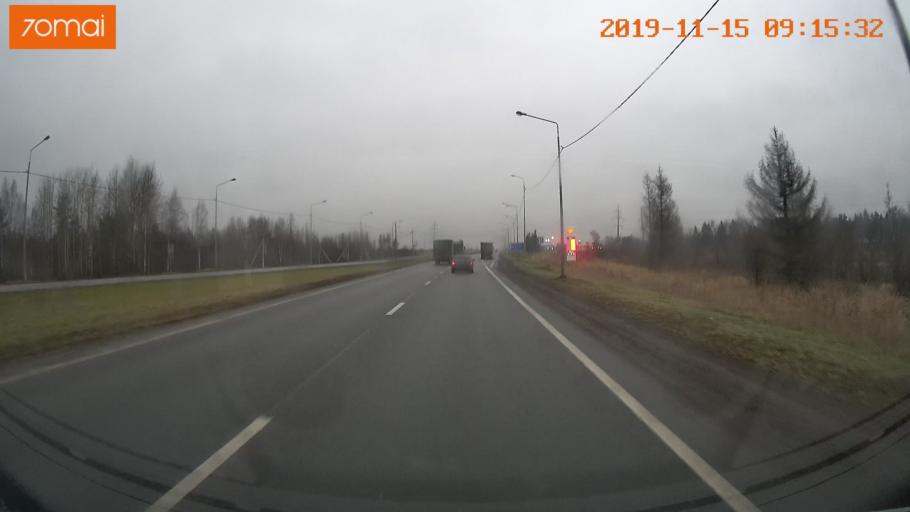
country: RU
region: Vologda
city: Tonshalovo
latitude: 59.2400
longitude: 37.9675
